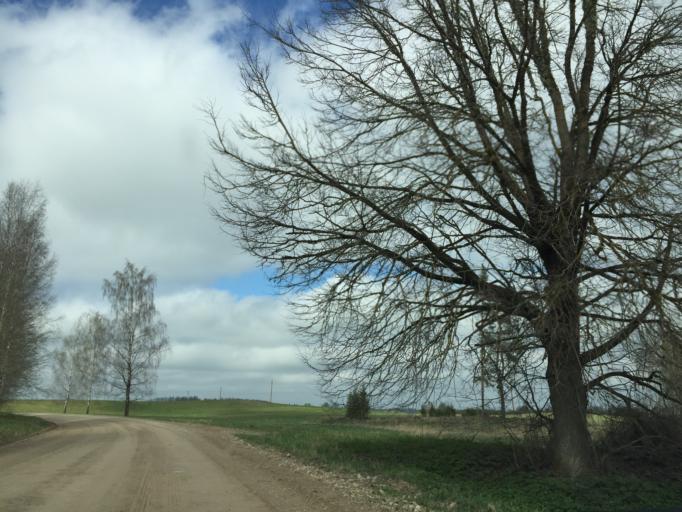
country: EE
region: Valgamaa
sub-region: Valga linn
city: Valga
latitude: 57.5430
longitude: 26.3147
